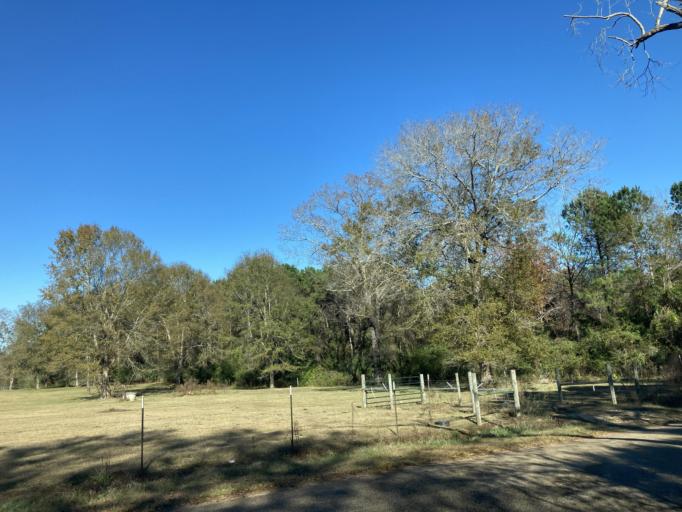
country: US
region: Mississippi
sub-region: Lamar County
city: Sumrall
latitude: 31.3425
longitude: -89.6503
